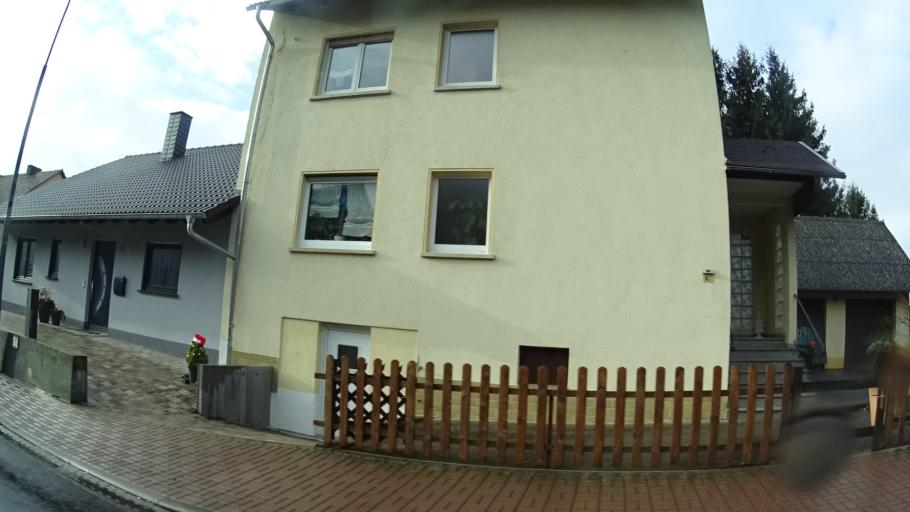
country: DE
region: Hesse
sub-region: Regierungsbezirk Kassel
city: Neuhof
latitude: 50.4530
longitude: 9.6223
